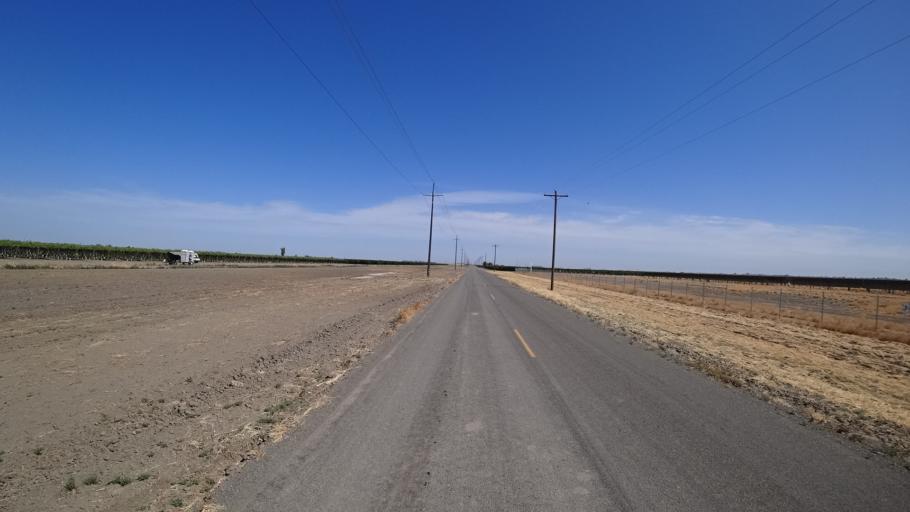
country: US
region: California
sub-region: Kings County
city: Stratford
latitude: 36.2459
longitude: -119.8344
